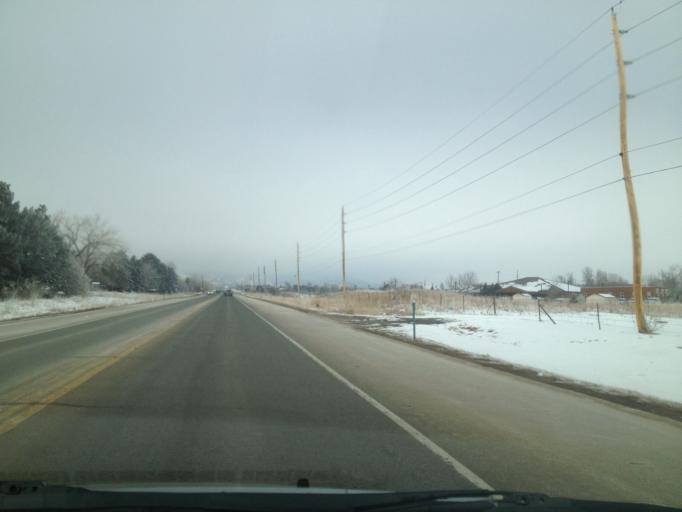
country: US
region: Colorado
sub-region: Boulder County
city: Boulder
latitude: 40.0563
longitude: -105.2676
